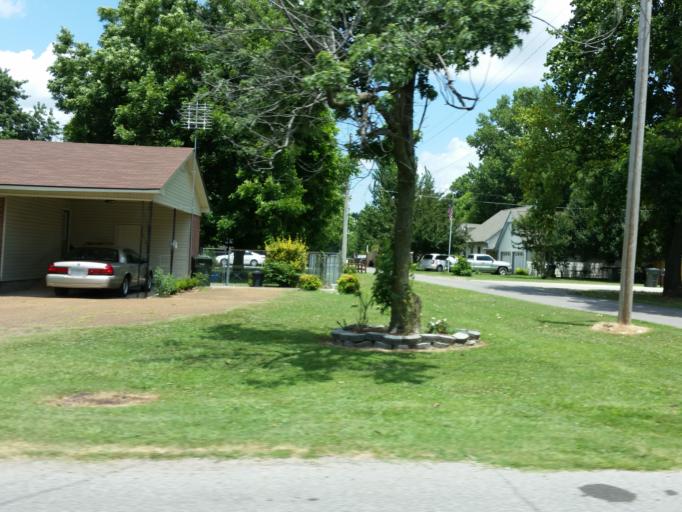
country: US
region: Tennessee
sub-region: Lake County
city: Tiptonville
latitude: 36.3737
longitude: -89.4706
